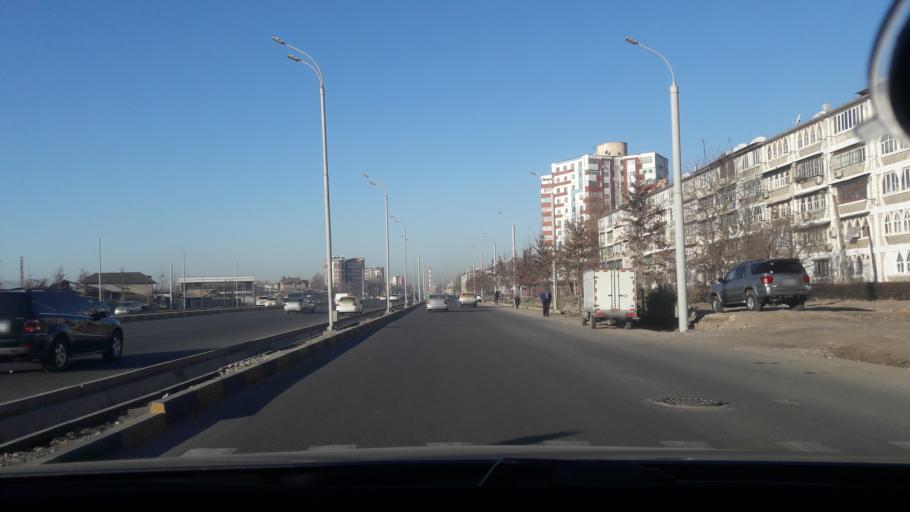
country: TJ
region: Dushanbe
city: Dushanbe
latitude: 38.5586
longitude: 68.7584
